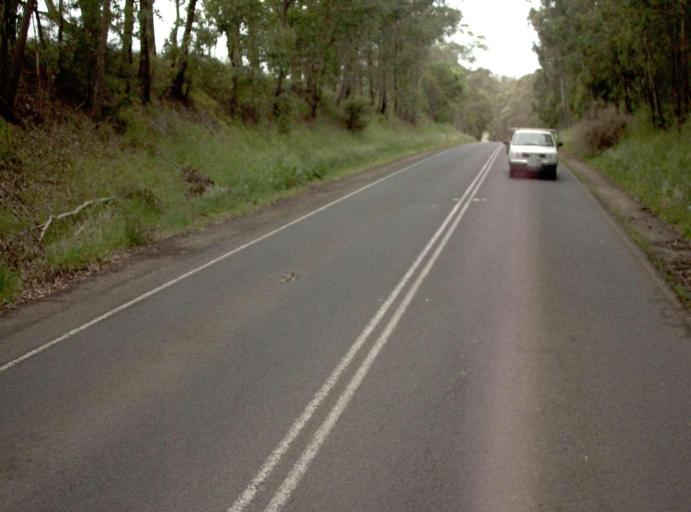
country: AU
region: Victoria
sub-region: Baw Baw
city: Warragul
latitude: -38.0763
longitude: 145.9656
